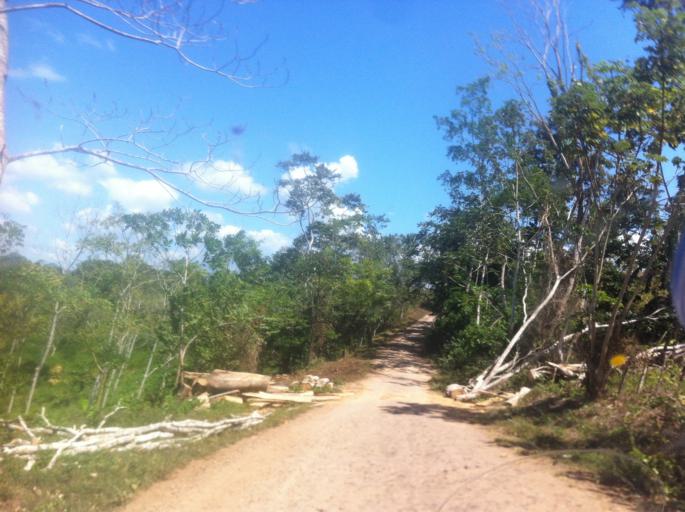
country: NI
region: Rio San Juan
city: San Carlos
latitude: 11.2380
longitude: -84.5227
